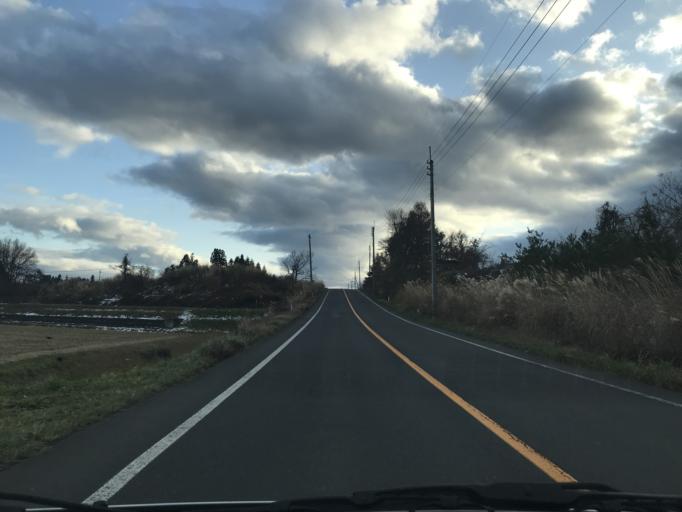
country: JP
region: Iwate
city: Mizusawa
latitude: 39.0888
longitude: 141.0514
